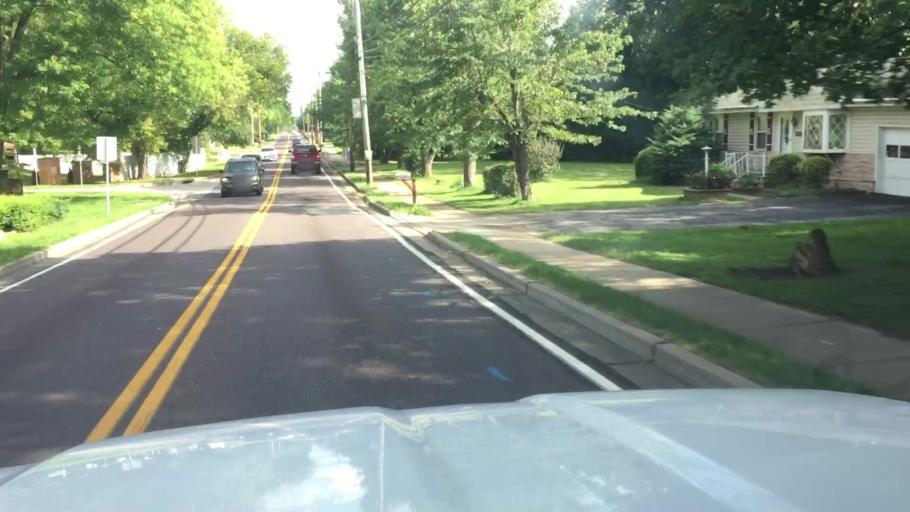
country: US
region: Missouri
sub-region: Jefferson County
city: Arnold
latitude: 38.4498
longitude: -90.3587
